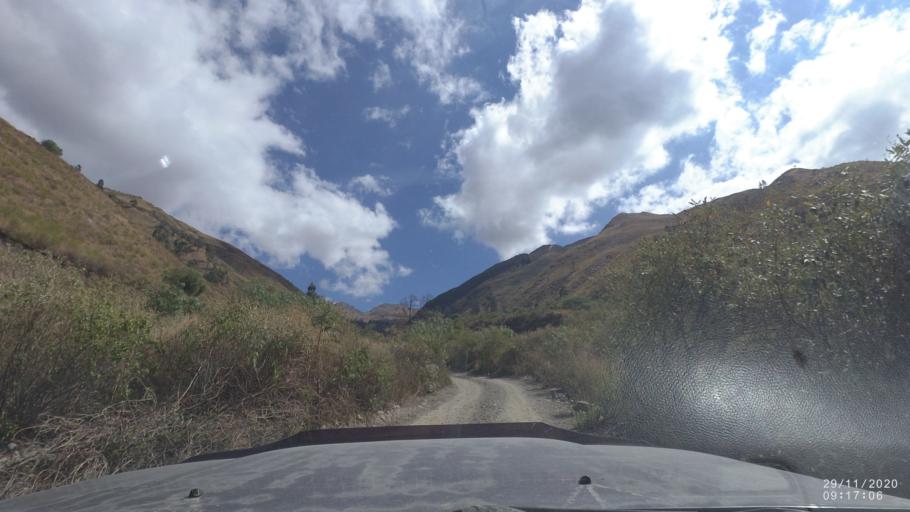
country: BO
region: Cochabamba
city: Cochabamba
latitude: -17.3253
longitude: -66.1845
